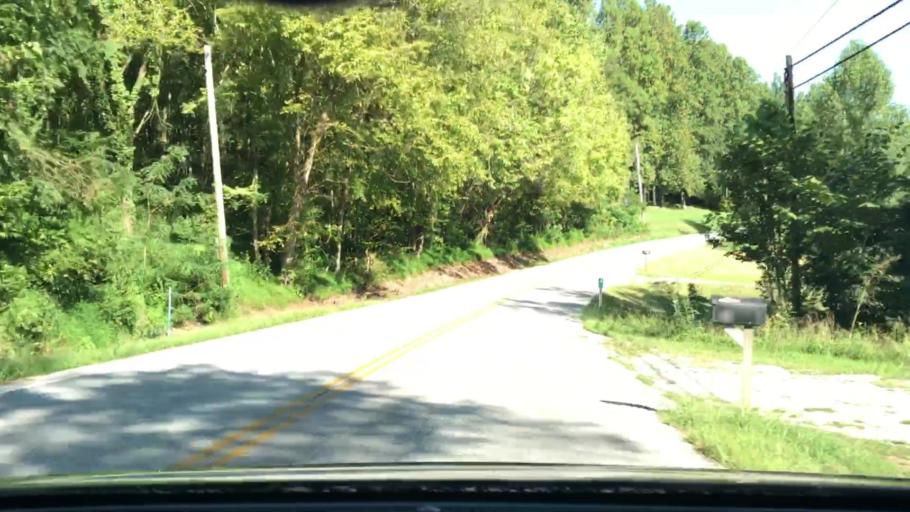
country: US
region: Tennessee
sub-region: Smith County
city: Carthage
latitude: 36.3077
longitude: -85.9514
